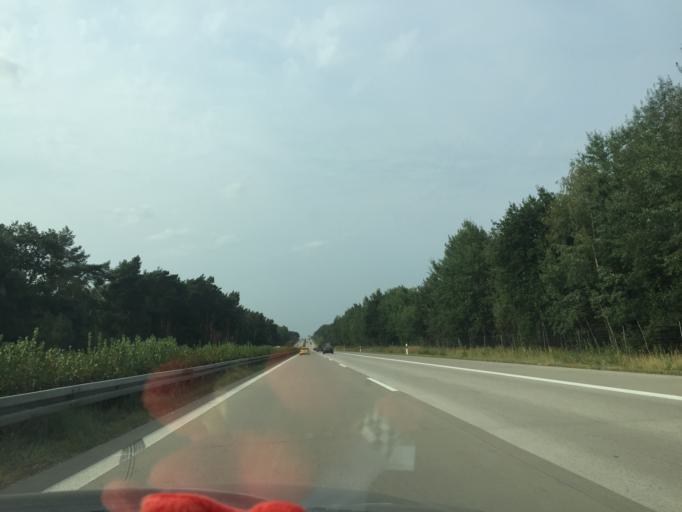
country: DE
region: Brandenburg
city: Bestensee
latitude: 52.2262
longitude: 13.5953
